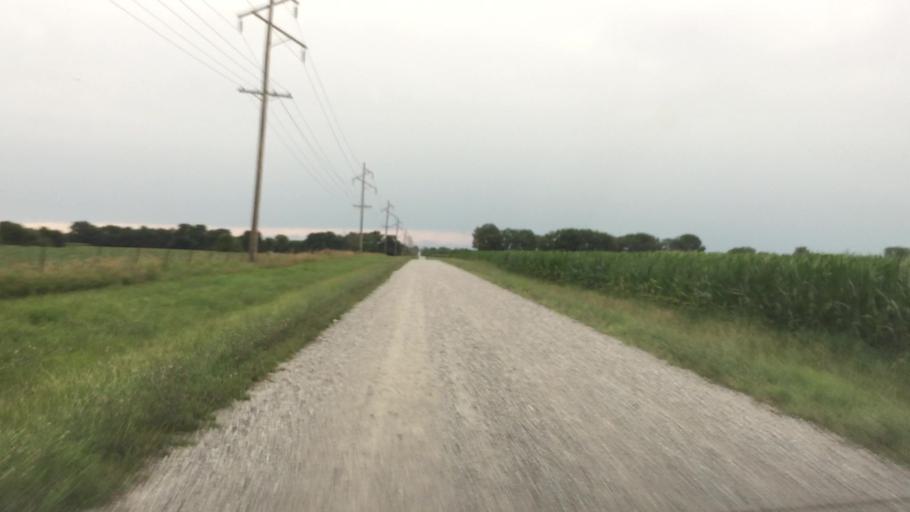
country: US
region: Illinois
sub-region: Hancock County
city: Hamilton
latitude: 40.4262
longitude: -91.3471
